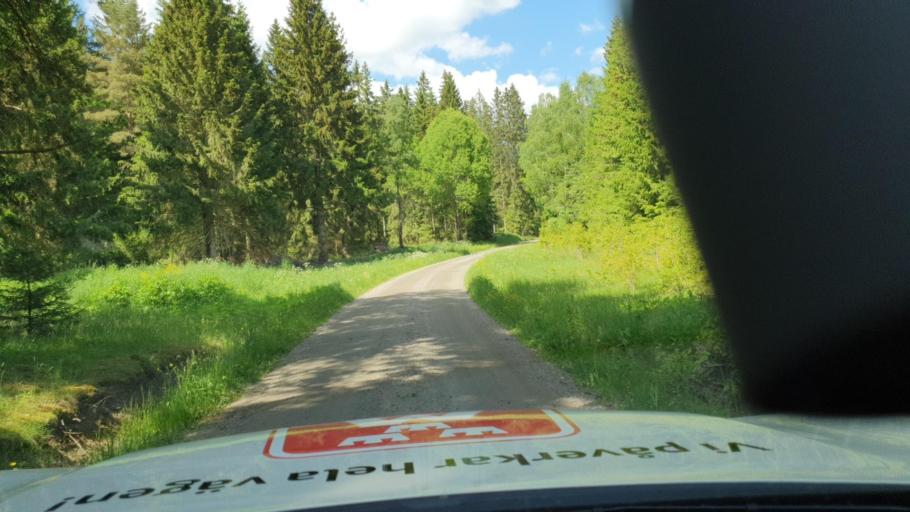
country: SE
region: Vaestra Goetaland
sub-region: Falkopings Kommun
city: Falkoeping
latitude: 58.0322
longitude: 13.6592
